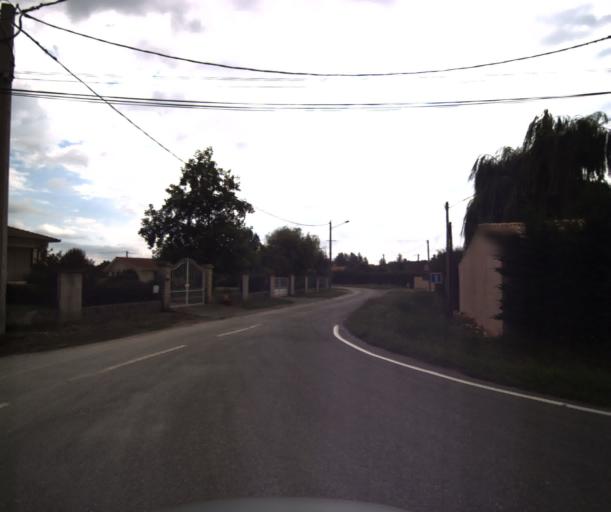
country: FR
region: Midi-Pyrenees
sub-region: Departement de la Haute-Garonne
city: Lacasse
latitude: 43.4017
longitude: 1.2585
